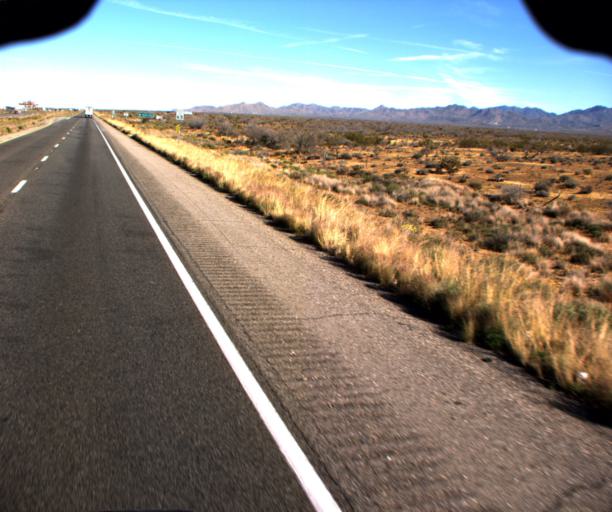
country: US
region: Arizona
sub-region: Mohave County
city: Golden Valley
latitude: 35.3297
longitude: -114.2106
